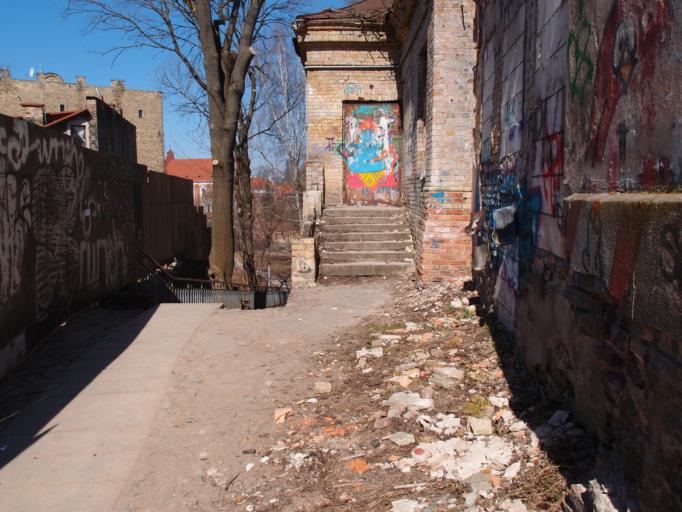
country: LT
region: Vilnius County
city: Rasos
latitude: 54.6812
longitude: 25.2976
